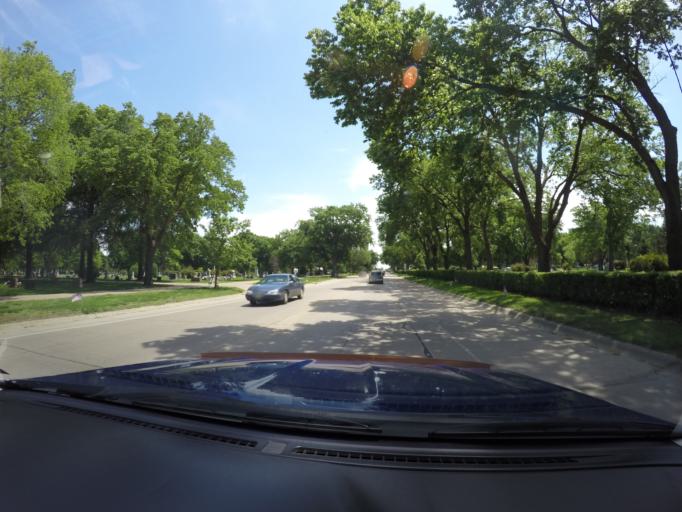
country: US
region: Nebraska
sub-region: Hall County
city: Grand Island
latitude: 40.9026
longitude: -98.3769
